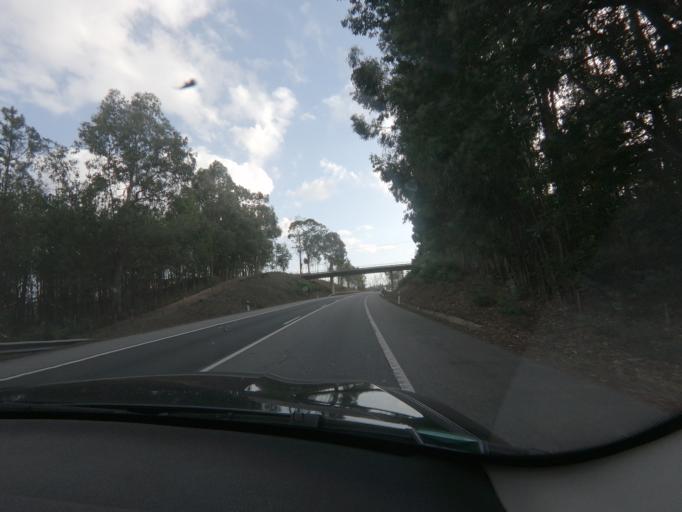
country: PT
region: Viseu
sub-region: Concelho de Tondela
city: Tondela
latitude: 40.5702
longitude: -8.0362
